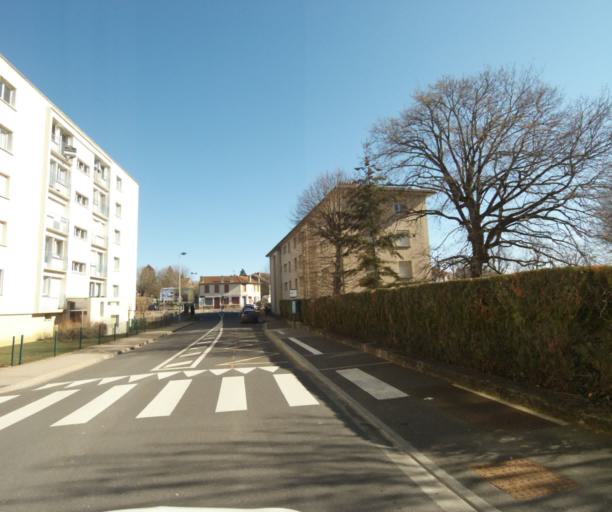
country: FR
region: Lorraine
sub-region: Departement de Meurthe-et-Moselle
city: Saint-Max
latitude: 48.7038
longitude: 6.2002
